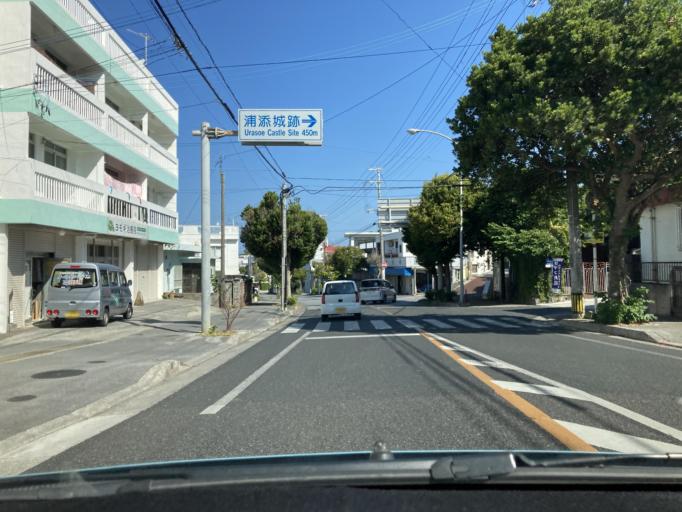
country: JP
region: Okinawa
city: Ginowan
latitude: 26.2490
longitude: 127.7264
